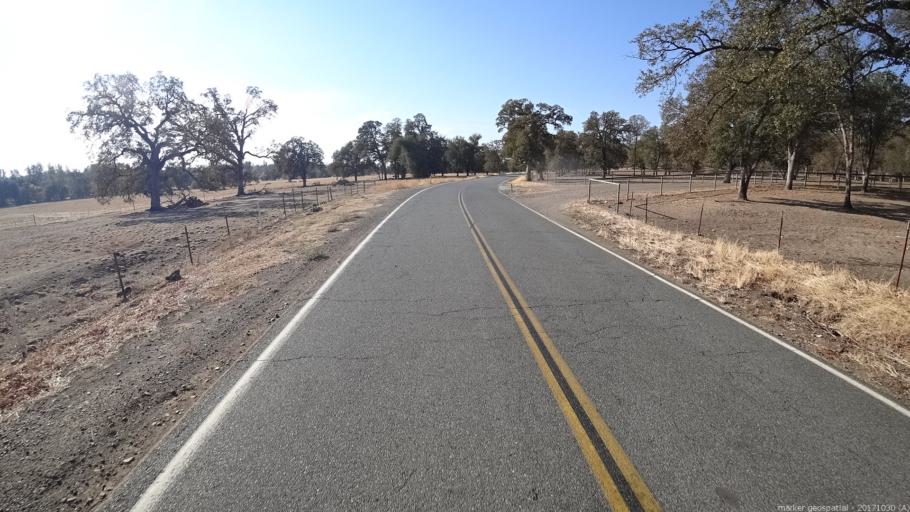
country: US
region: California
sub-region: Shasta County
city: Palo Cedro
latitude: 40.5776
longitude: -122.1829
